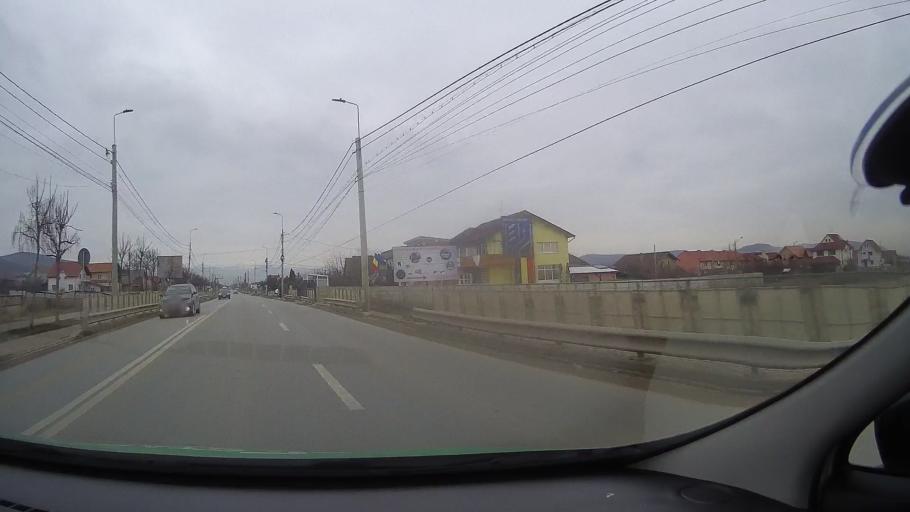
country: RO
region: Alba
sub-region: Municipiul Alba Iulia
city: Micesti
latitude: 46.0919
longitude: 23.5549
